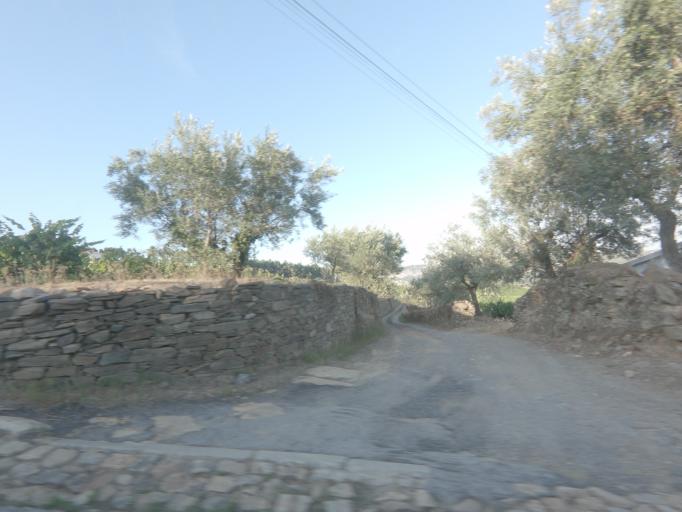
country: PT
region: Vila Real
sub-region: Sabrosa
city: Sabrosa
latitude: 41.2666
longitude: -7.5681
